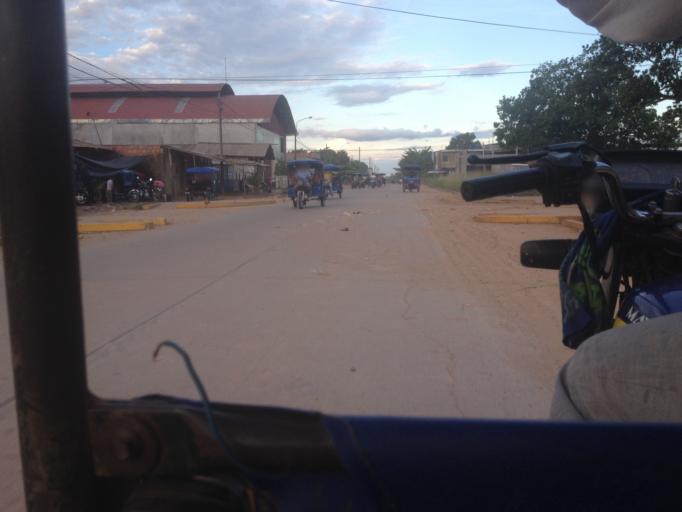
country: PE
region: Ucayali
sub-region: Provincia de Coronel Portillo
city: Pucallpa
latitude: -8.3820
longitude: -74.5643
